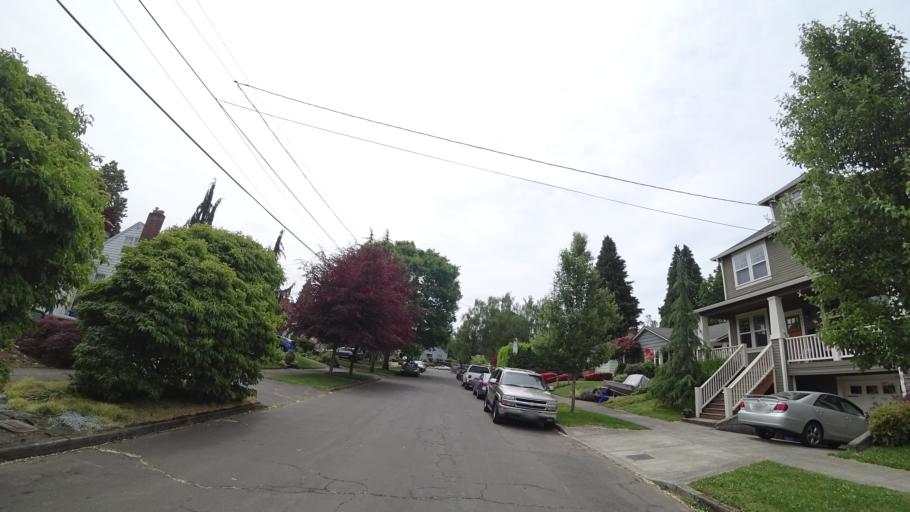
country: US
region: Oregon
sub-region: Multnomah County
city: Portland
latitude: 45.5673
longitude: -122.6286
